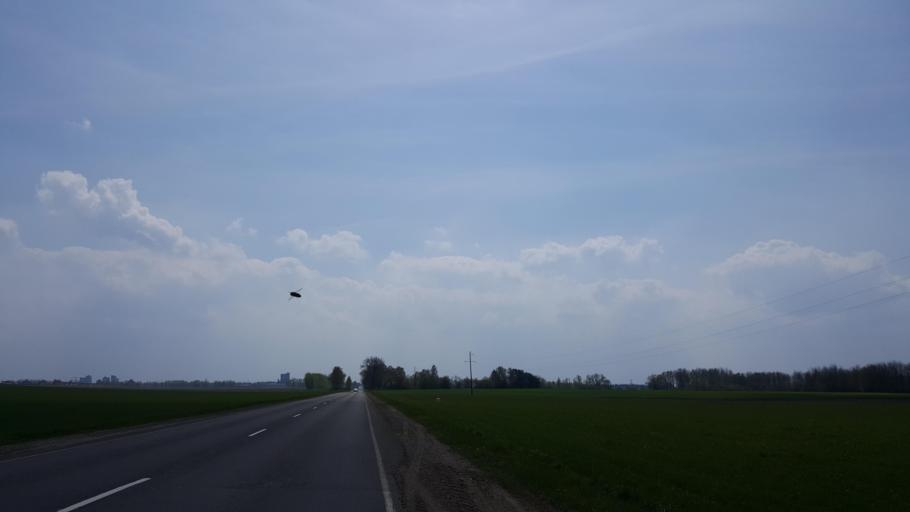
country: BY
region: Brest
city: Zhabinka
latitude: 52.2258
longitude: 23.9885
